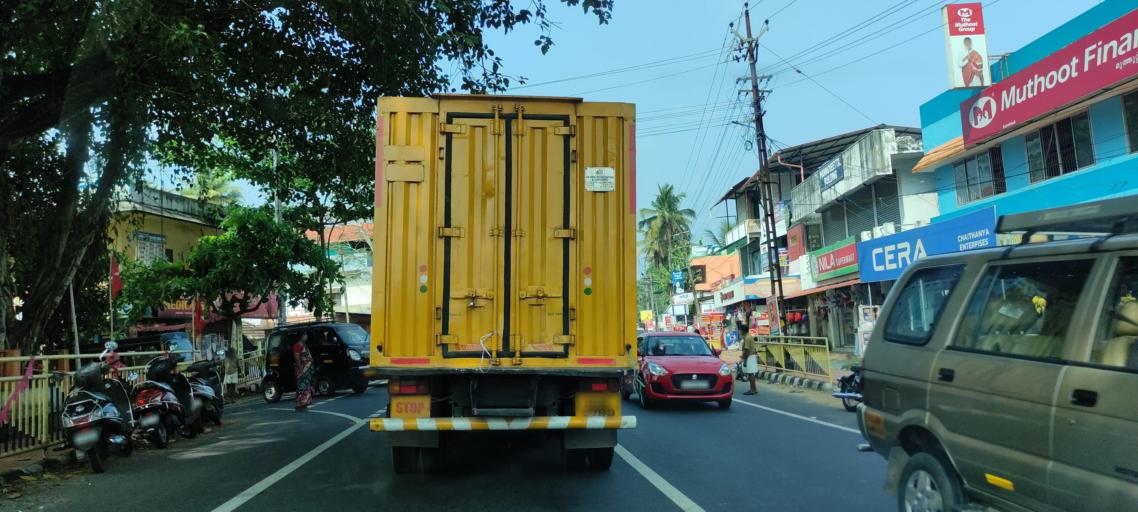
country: IN
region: Kerala
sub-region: Alappuzha
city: Chengannur
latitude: 9.2726
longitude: 76.6551
